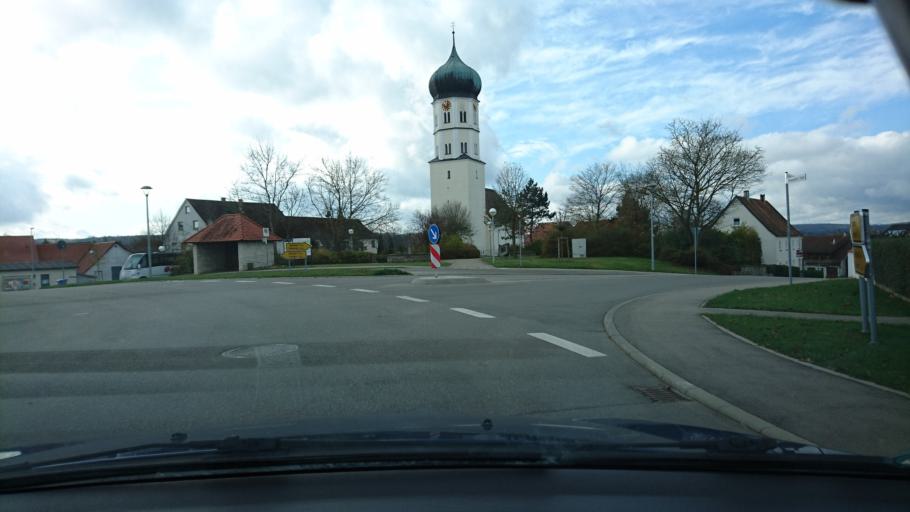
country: DE
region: Bavaria
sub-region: Swabia
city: Forheim
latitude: 48.7582
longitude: 10.4106
